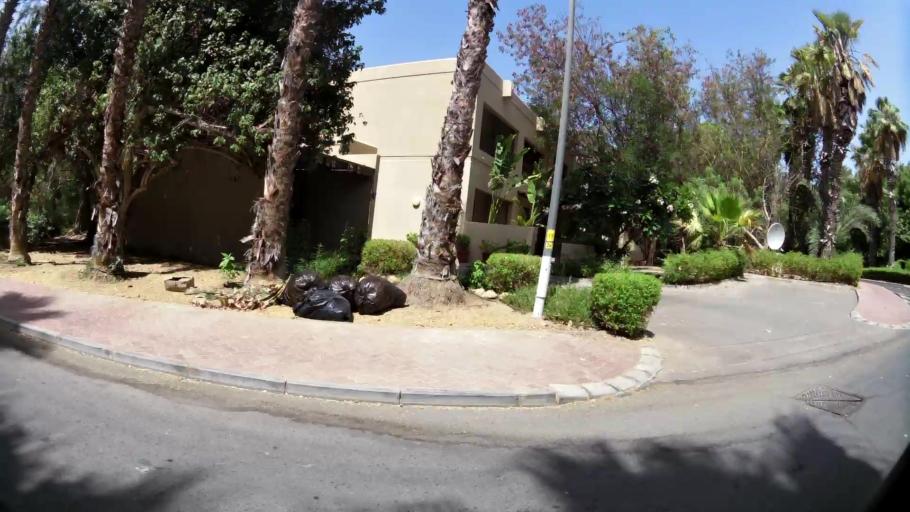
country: OM
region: Muhafazat Masqat
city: Muscat
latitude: 23.6334
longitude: 58.4916
